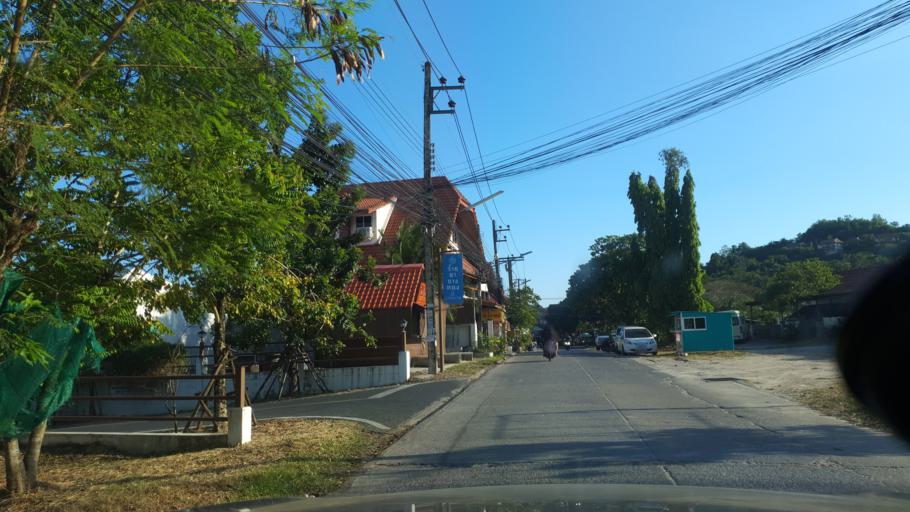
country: TH
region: Phuket
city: Kathu
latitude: 7.9039
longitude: 98.3300
